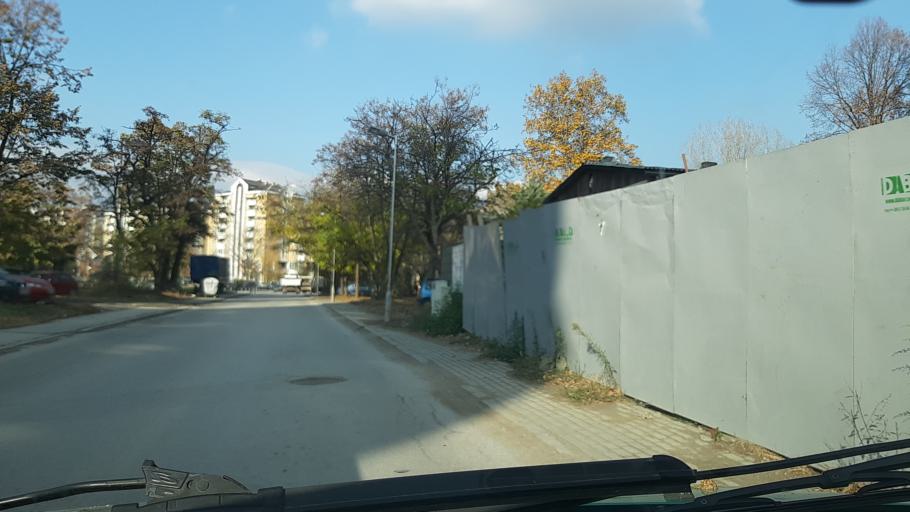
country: MK
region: Karpos
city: Skopje
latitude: 41.9860
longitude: 21.4524
